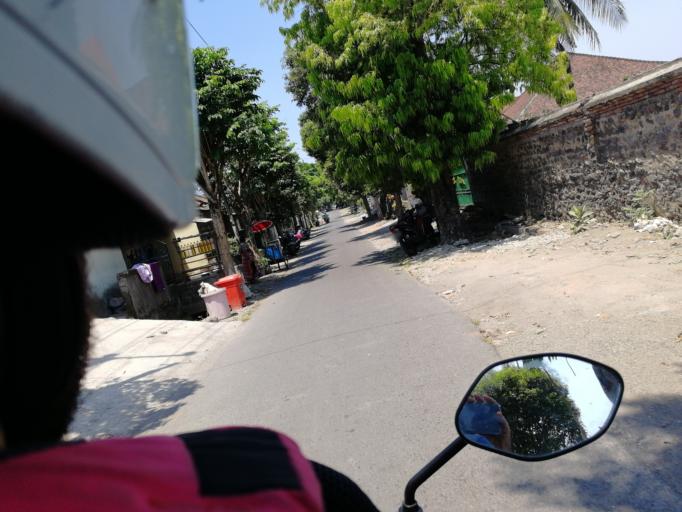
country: ID
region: Bali
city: Subagan
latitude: -8.4571
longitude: 115.5966
